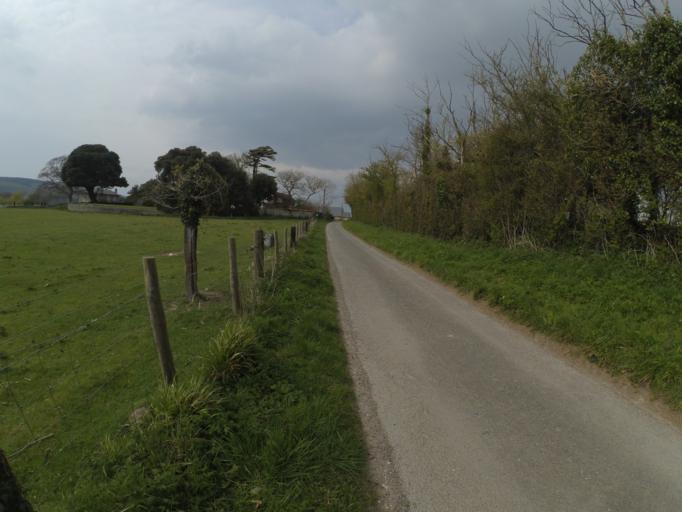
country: GB
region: England
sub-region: West Sussex
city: Arundel
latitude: 50.8730
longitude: -0.5267
